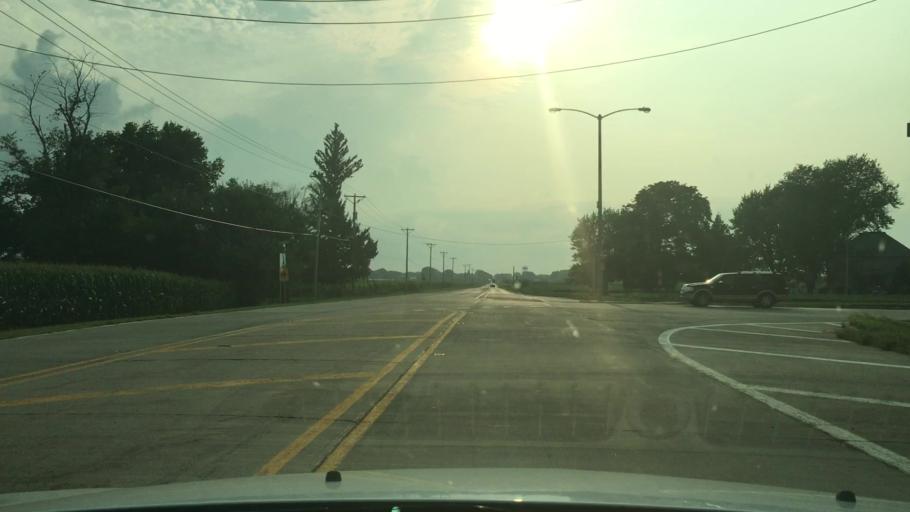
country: US
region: Illinois
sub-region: Ogle County
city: Rochelle
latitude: 41.9200
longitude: -89.0329
